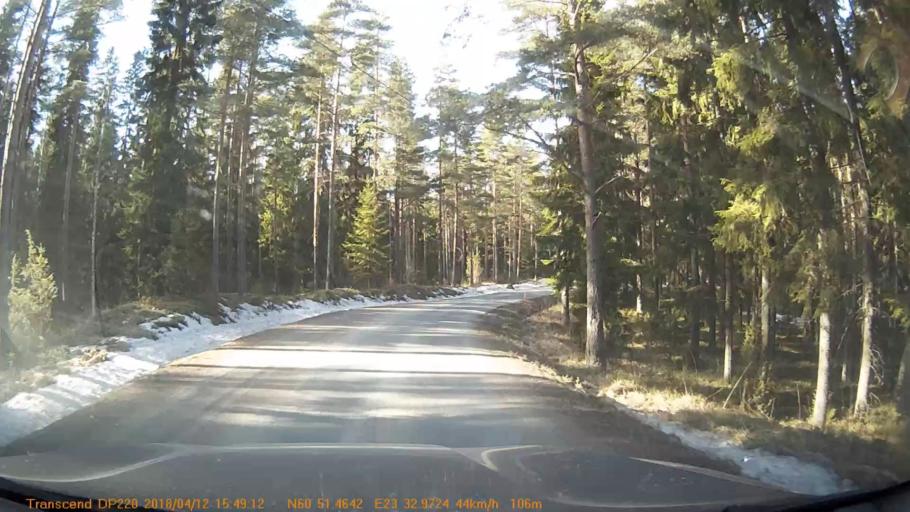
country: FI
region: Haeme
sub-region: Forssa
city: Forssa
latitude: 60.8580
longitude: 23.5493
